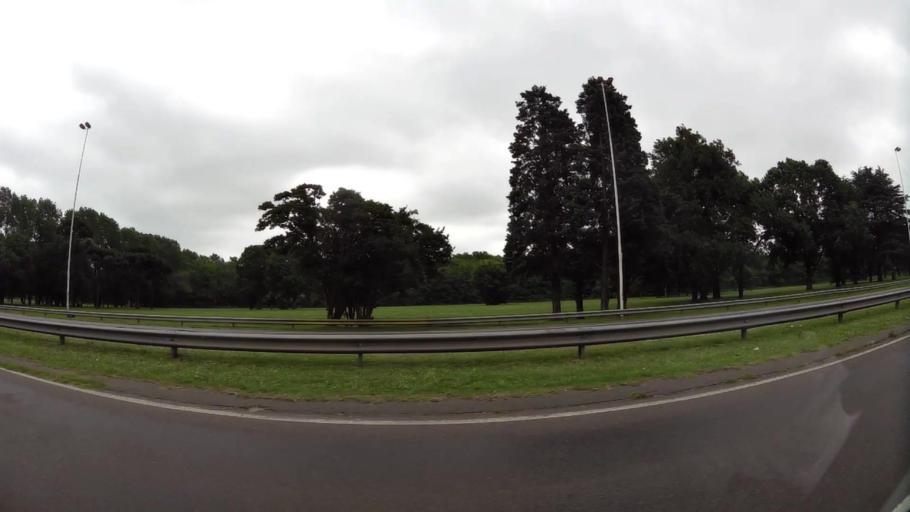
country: AR
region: Buenos Aires
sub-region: Partido de Ezeiza
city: Ezeiza
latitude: -34.7992
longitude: -58.5346
